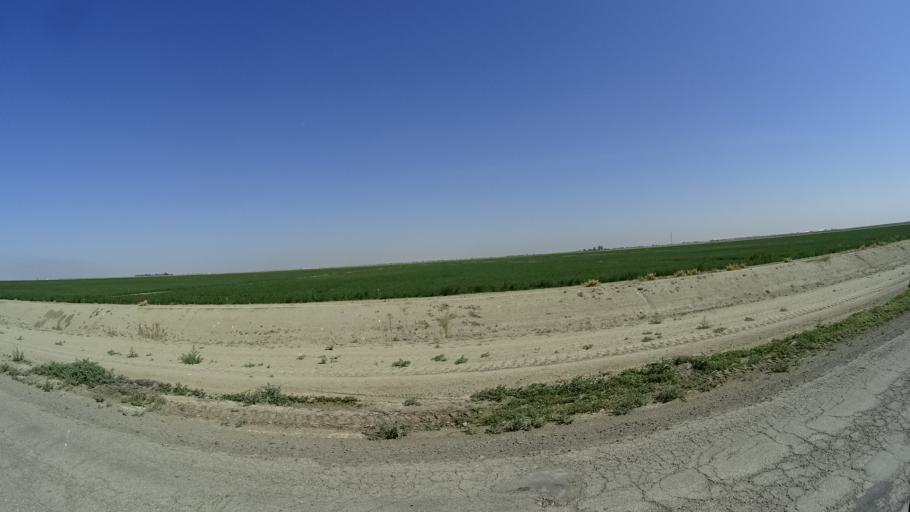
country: US
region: California
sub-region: Kings County
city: Corcoran
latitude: 36.0072
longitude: -119.5491
